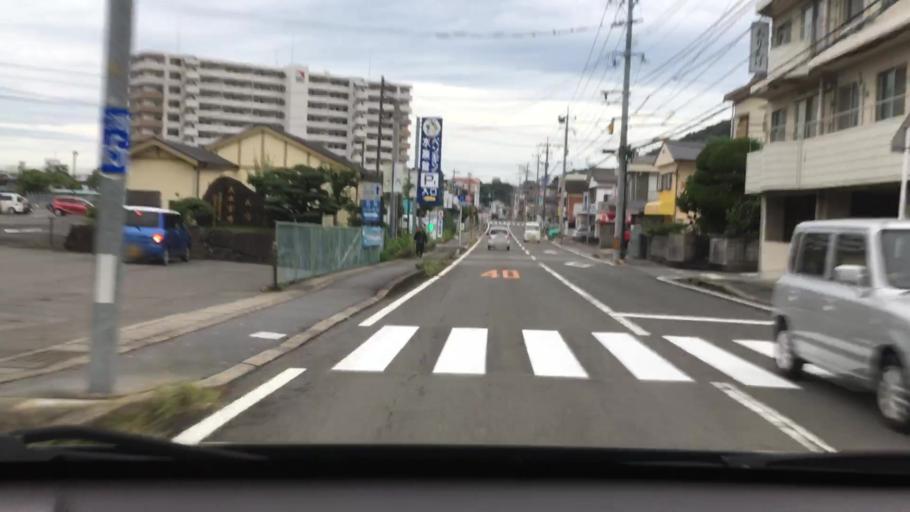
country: JP
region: Nagasaki
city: Nagasaki-shi
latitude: 32.7580
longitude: 129.9432
